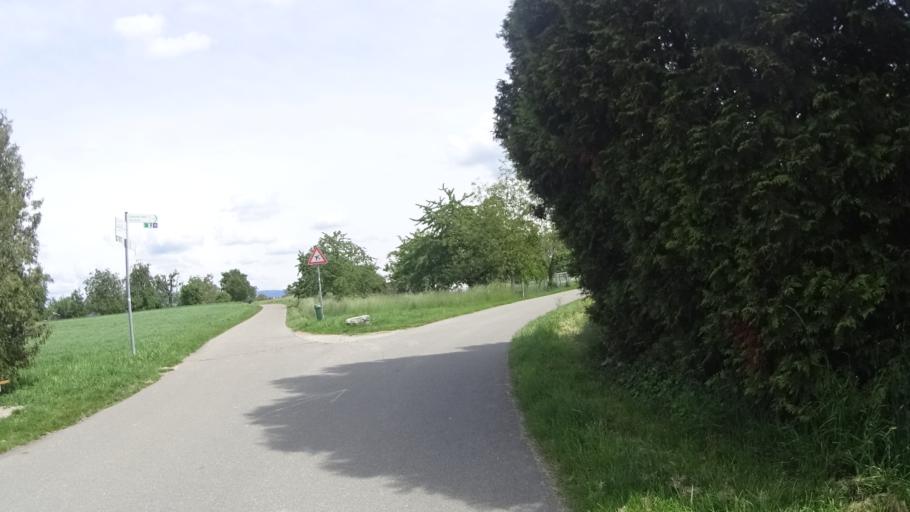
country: CH
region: Aargau
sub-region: Bezirk Rheinfelden
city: Kaiseraugst
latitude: 47.5565
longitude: 7.7393
